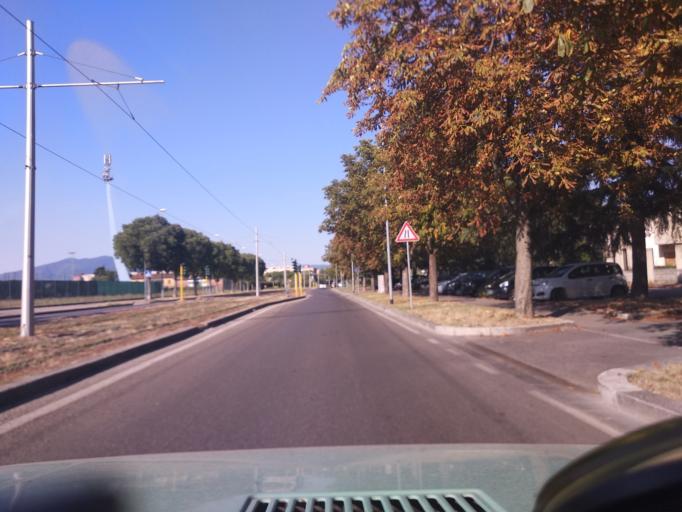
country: IT
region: Tuscany
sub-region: Province of Florence
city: Scandicci
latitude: 43.7597
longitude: 11.1841
